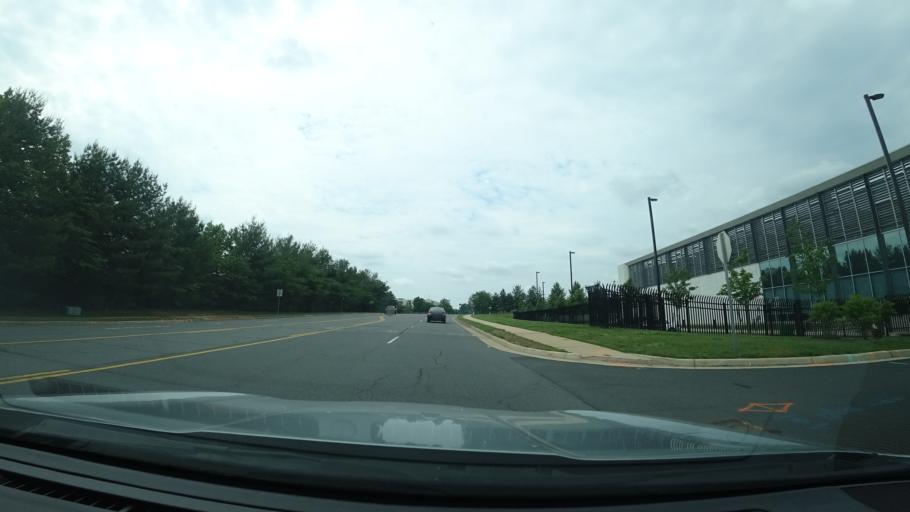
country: US
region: Virginia
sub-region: Loudoun County
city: Dulles Town Center
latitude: 39.0254
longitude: -77.4136
